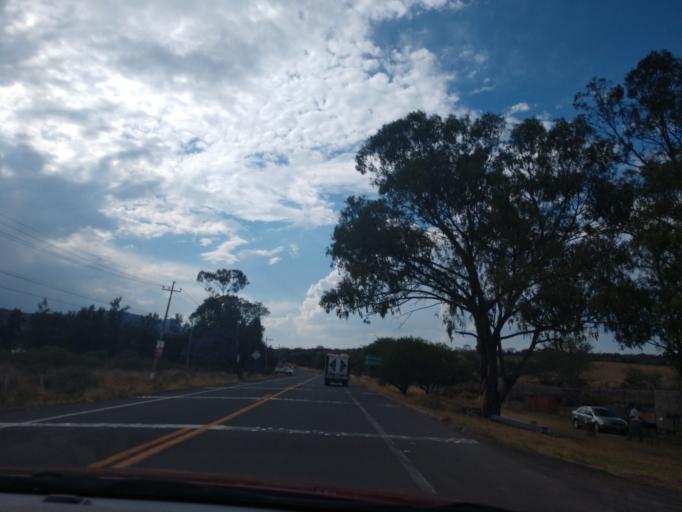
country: MX
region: Jalisco
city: Chapala
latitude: 20.1537
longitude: -103.1873
